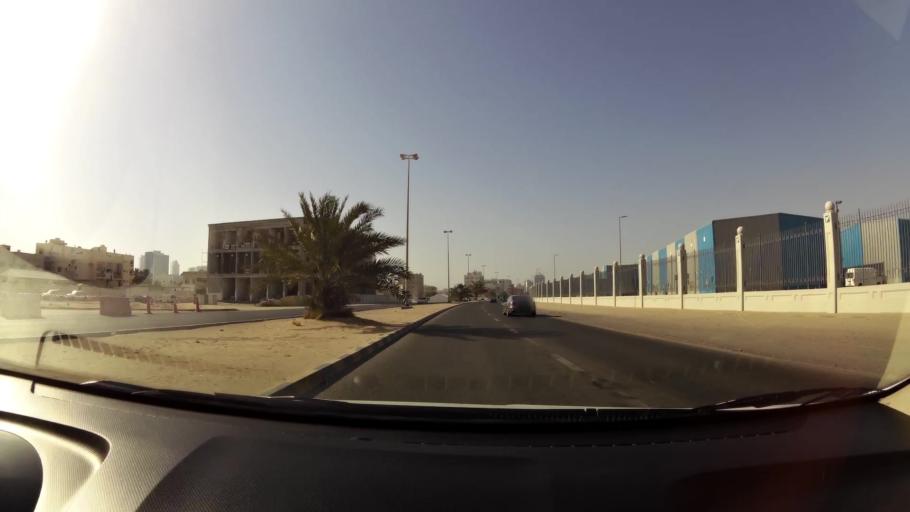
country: AE
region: Ajman
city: Ajman
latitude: 25.4058
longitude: 55.4517
